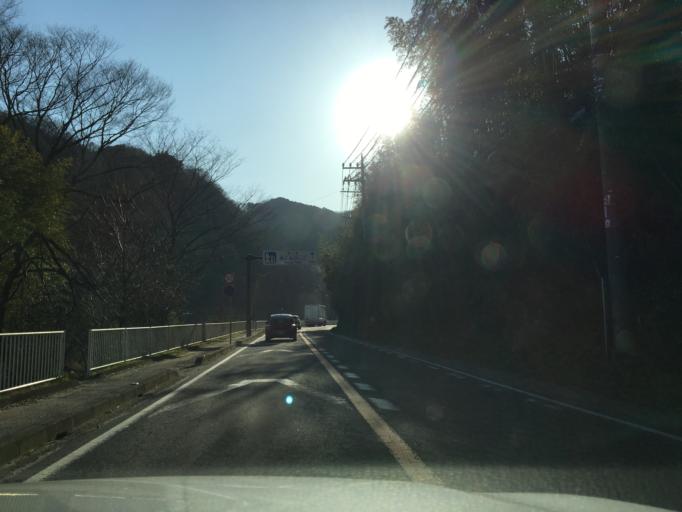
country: JP
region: Ibaraki
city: Daigo
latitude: 36.7613
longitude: 140.3678
